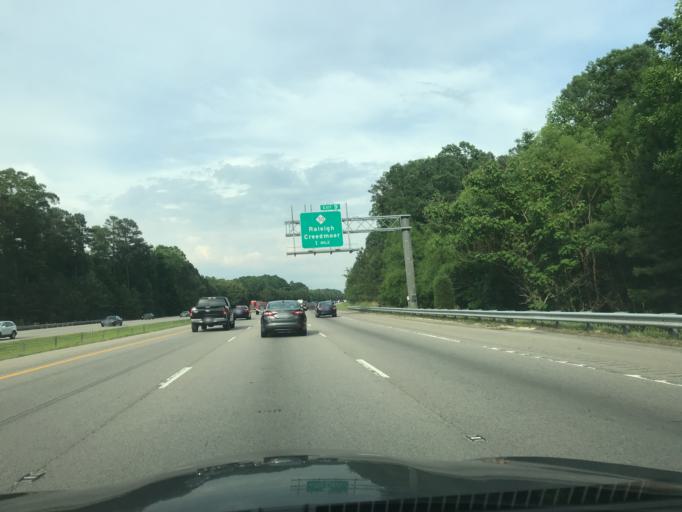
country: US
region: North Carolina
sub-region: Wake County
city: West Raleigh
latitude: 35.9154
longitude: -78.7060
